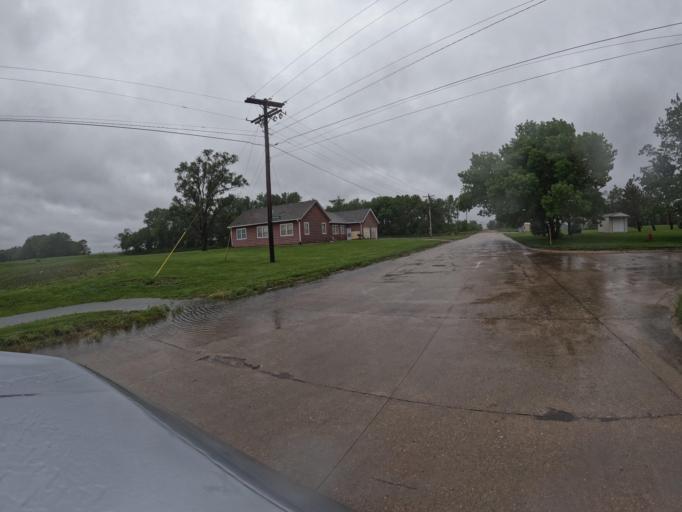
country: US
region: Nebraska
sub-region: Saline County
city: Wilber
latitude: 40.3965
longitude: -96.9324
